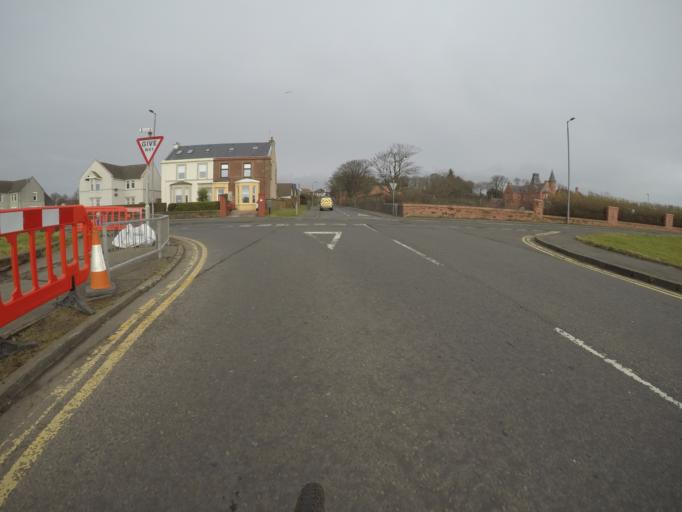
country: GB
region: Scotland
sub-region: North Ayrshire
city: Ardrossan
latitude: 55.6517
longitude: -4.8188
